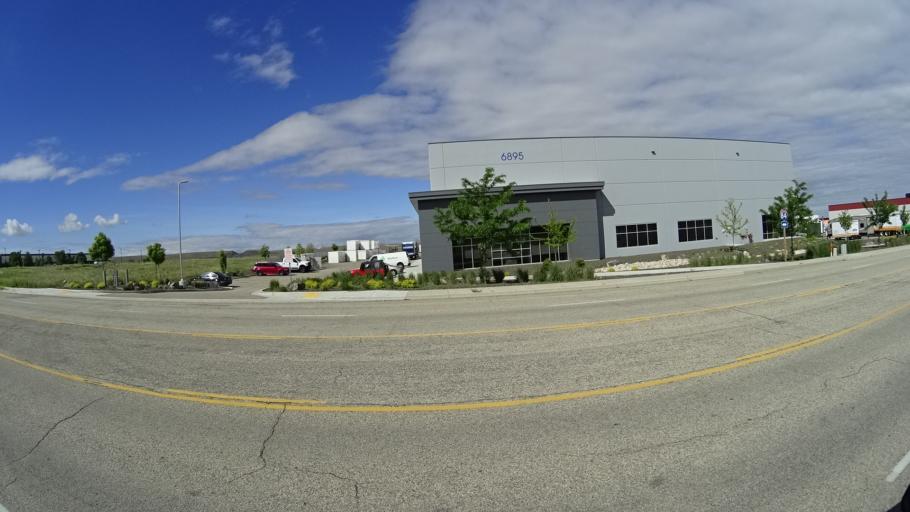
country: US
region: Idaho
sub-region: Ada County
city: Boise
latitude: 43.5398
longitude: -116.1637
